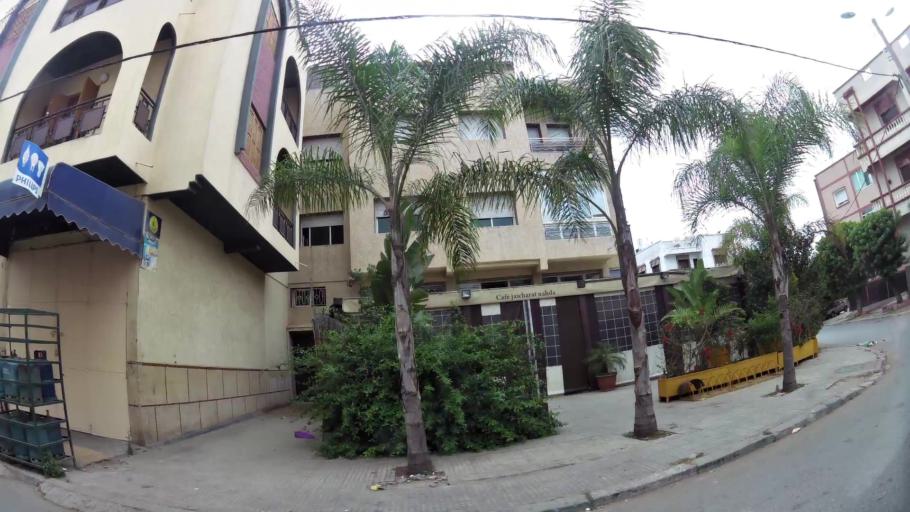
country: MA
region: Rabat-Sale-Zemmour-Zaer
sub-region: Rabat
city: Rabat
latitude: 33.9798
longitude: -6.8193
